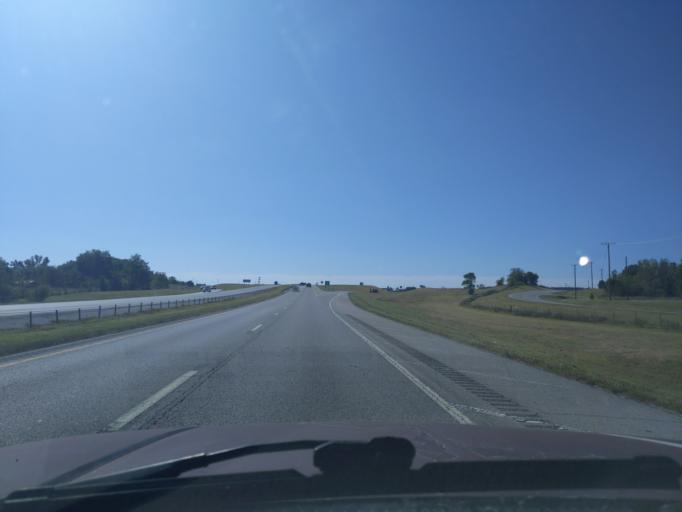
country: US
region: Oklahoma
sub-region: Tulsa County
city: Glenpool
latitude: 35.9932
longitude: -96.0118
